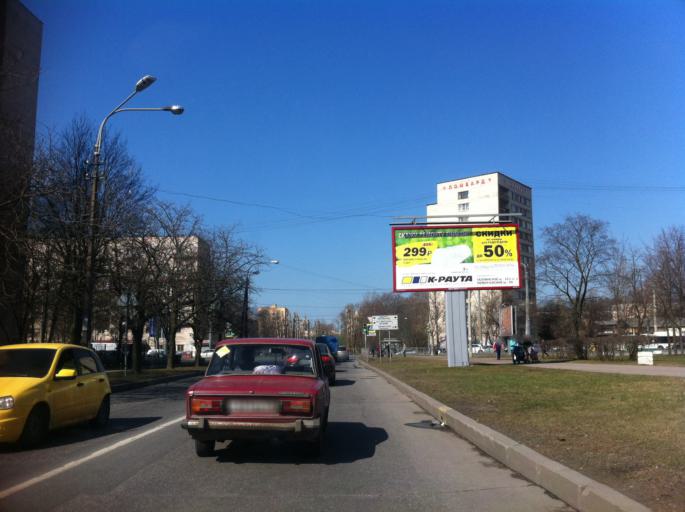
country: RU
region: St.-Petersburg
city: Dachnoye
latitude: 59.8416
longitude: 30.2455
